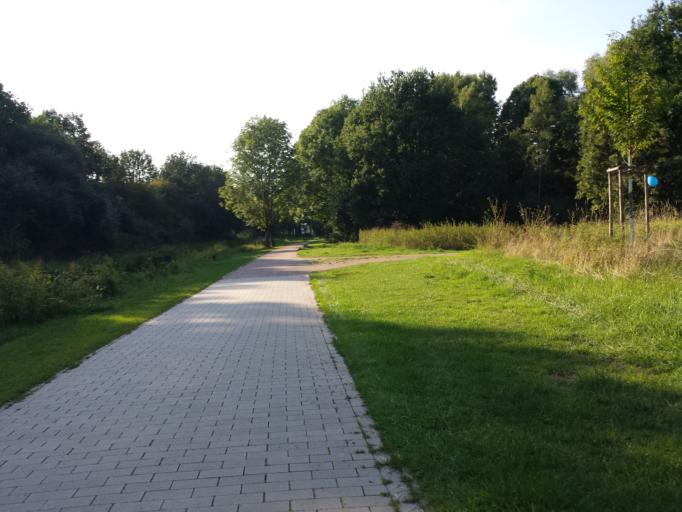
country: DE
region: Bremen
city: Bremen
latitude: 53.0461
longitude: 8.8284
